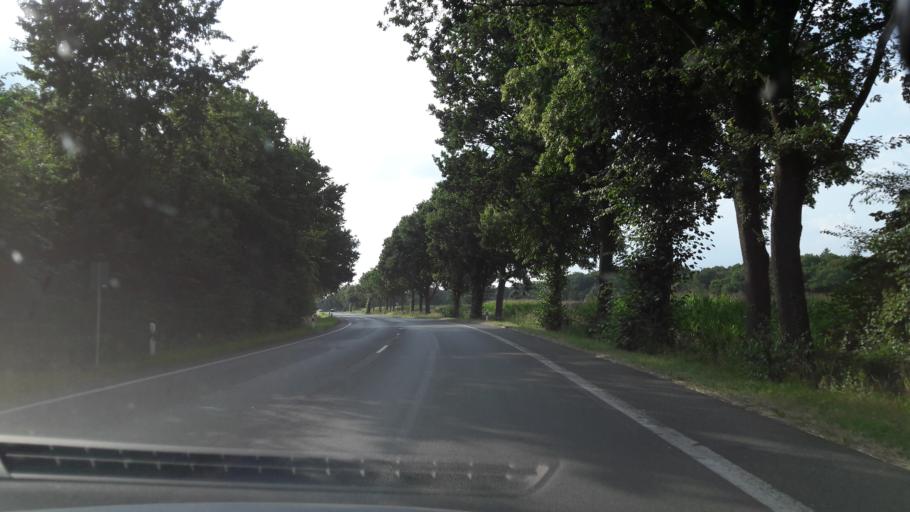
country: DE
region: North Rhine-Westphalia
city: Ahlen
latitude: 51.8120
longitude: 7.9363
